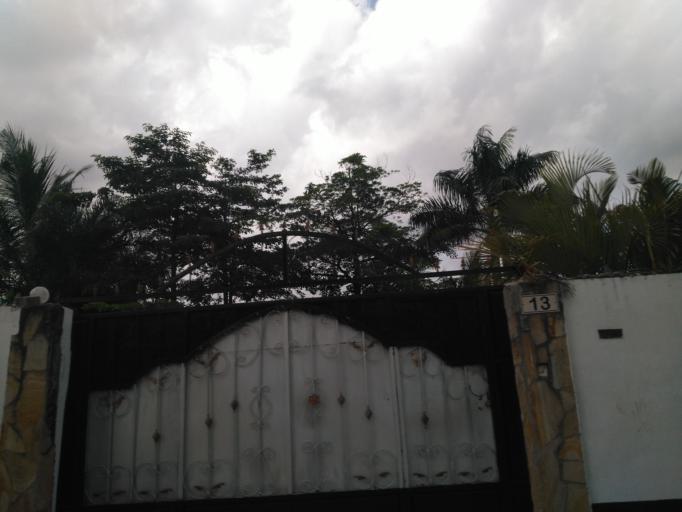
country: TZ
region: Dar es Salaam
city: Magomeni
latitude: -6.7633
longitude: 39.2474
